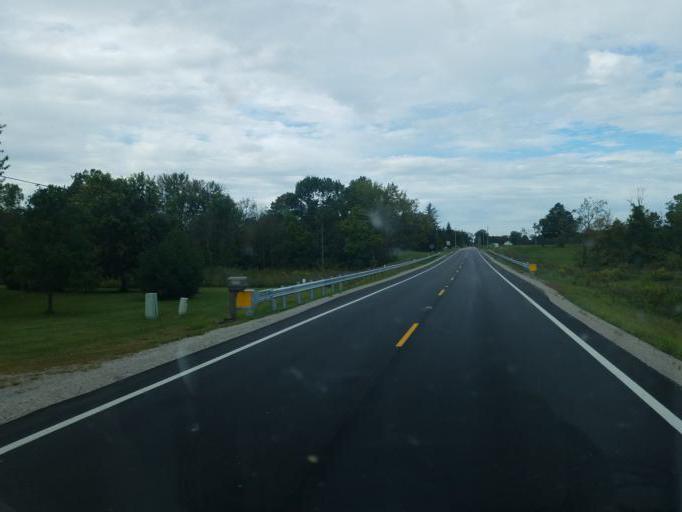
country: US
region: Ohio
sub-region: Franklin County
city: New Albany
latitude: 40.1262
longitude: -82.8101
